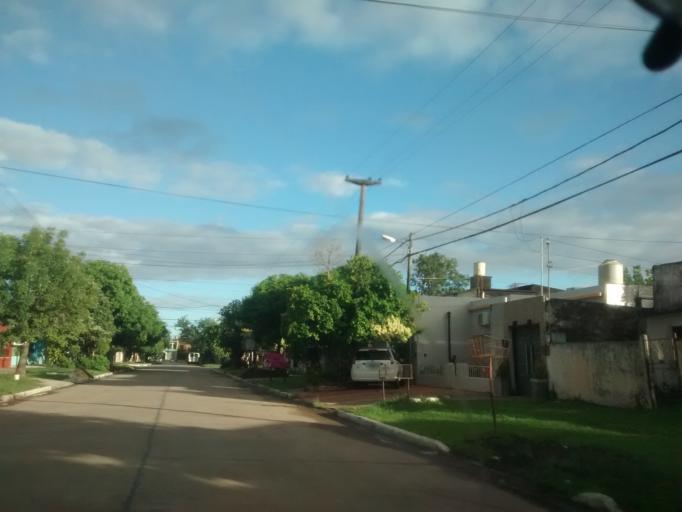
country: AR
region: Chaco
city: Resistencia
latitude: -27.4621
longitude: -58.9956
